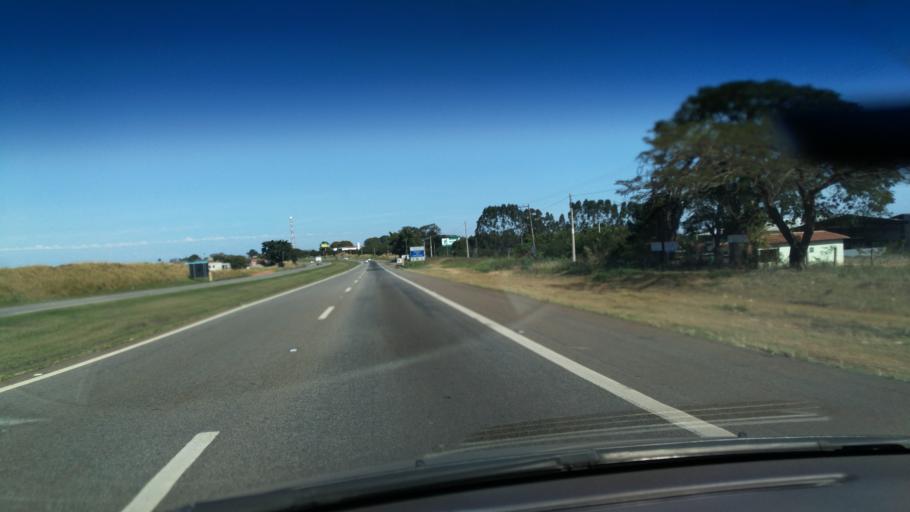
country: BR
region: Sao Paulo
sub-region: Mogi-Mirim
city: Mogi Mirim
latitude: -22.5099
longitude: -46.9887
